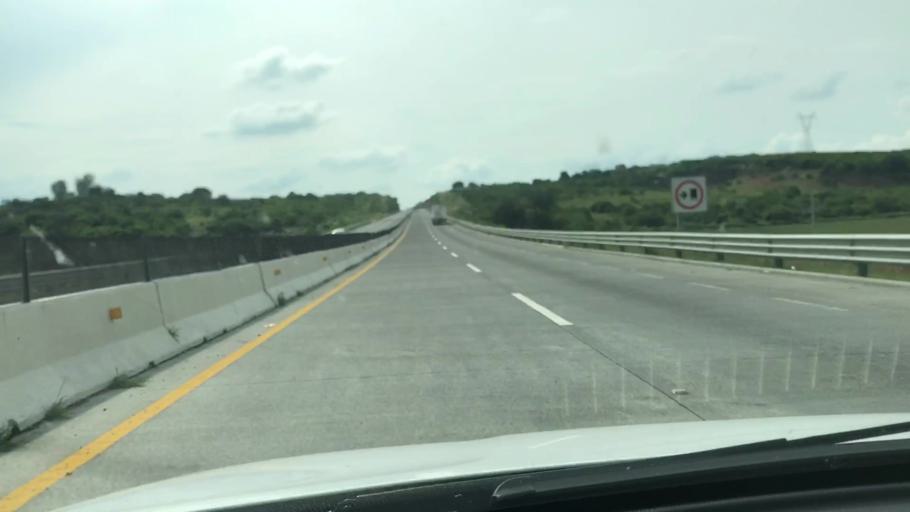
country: MX
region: Guanajuato
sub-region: Penjamo
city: Estacion la Piedad
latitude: 20.4002
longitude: -102.0171
